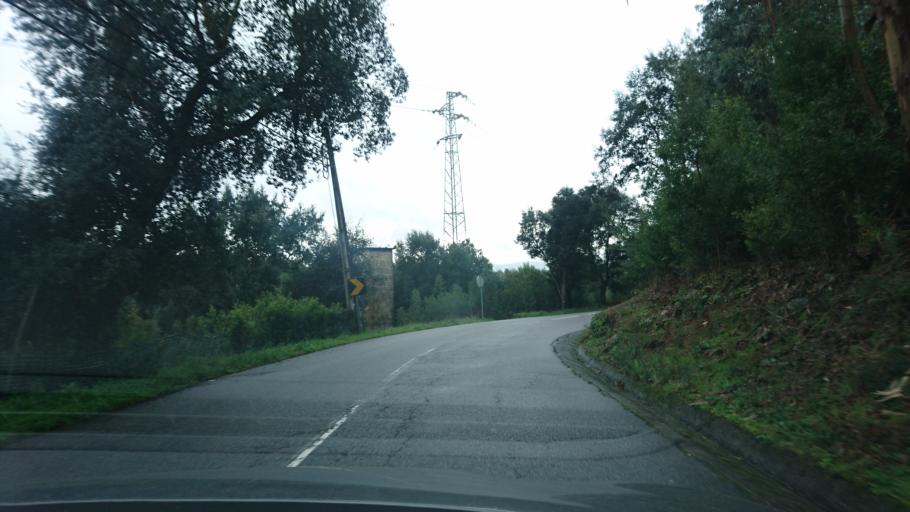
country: PT
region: Porto
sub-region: Paredes
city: Baltar
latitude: 41.1663
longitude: -8.3830
